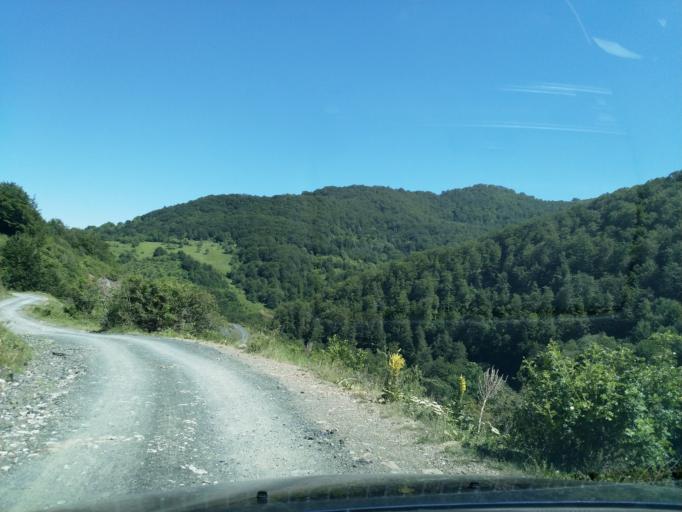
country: XK
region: Mitrovica
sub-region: Komuna e Leposaviqit
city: Leposaviq
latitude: 43.2647
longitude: 20.8623
